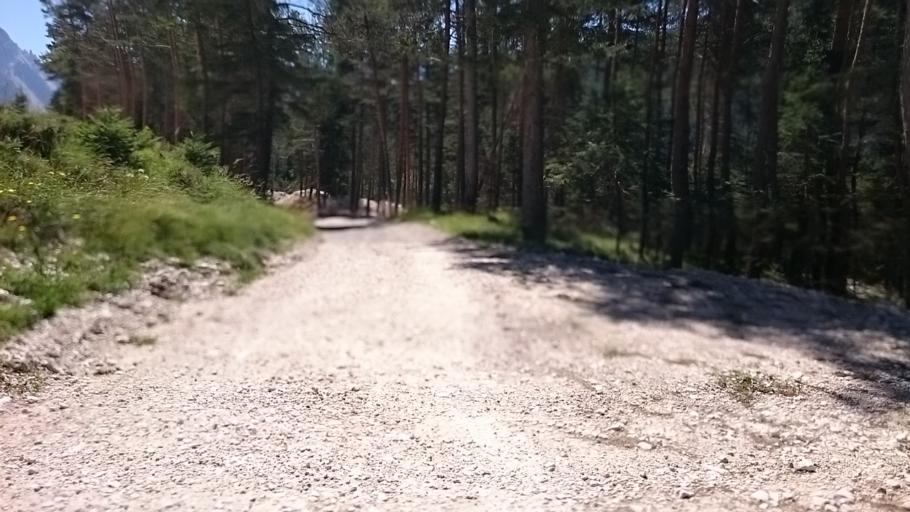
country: IT
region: Veneto
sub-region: Provincia di Belluno
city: Cortina d'Ampezzo
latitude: 46.5007
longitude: 12.1653
